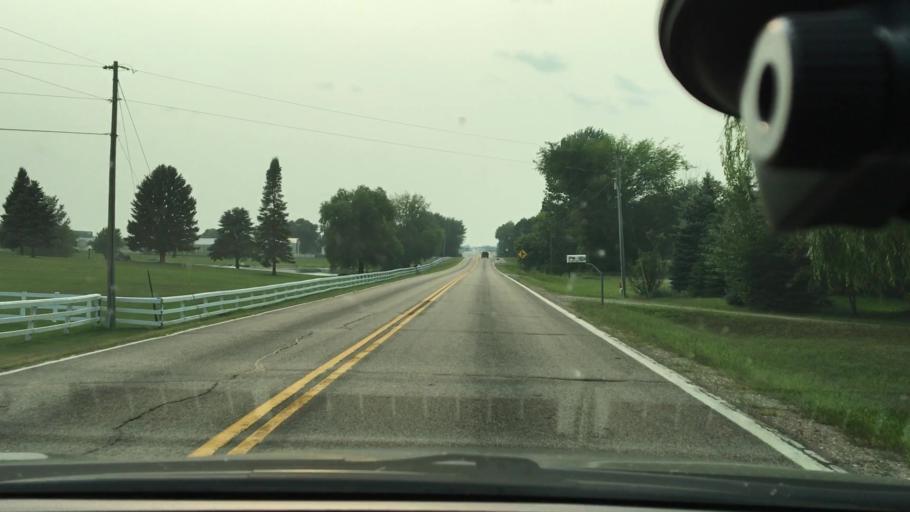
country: US
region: Minnesota
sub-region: Hennepin County
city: Dayton
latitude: 45.2523
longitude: -93.5426
